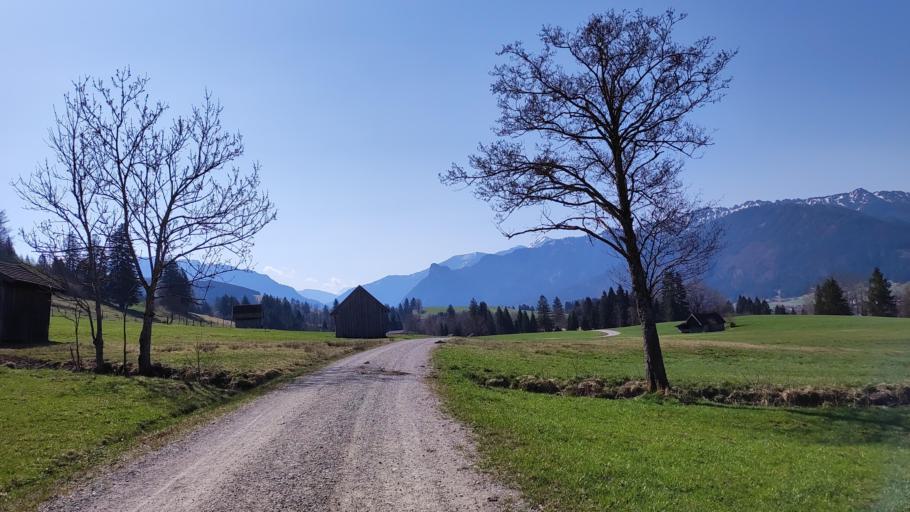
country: DE
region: Bavaria
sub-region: Upper Bavaria
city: Unterammergau
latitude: 47.6341
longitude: 11.0350
